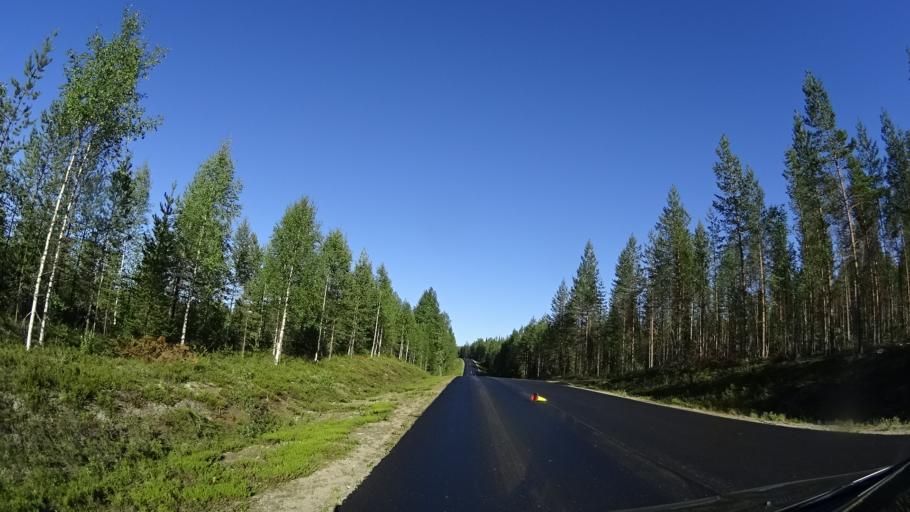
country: FI
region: North Karelia
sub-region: Pielisen Karjala
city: Valtimo
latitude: 63.5615
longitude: 28.5917
